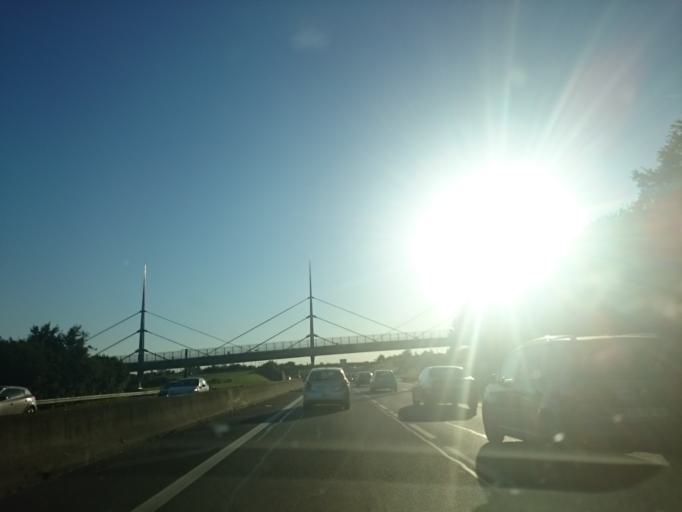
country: FR
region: Brittany
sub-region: Departement d'Ille-et-Vilaine
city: Chantepie
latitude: 48.0852
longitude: -1.6395
